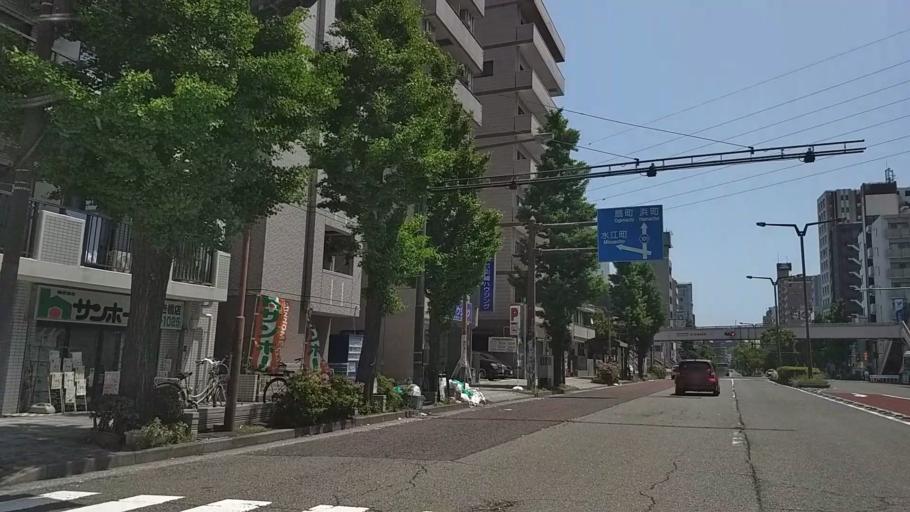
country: JP
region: Kanagawa
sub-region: Kawasaki-shi
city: Kawasaki
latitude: 35.5249
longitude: 139.7066
